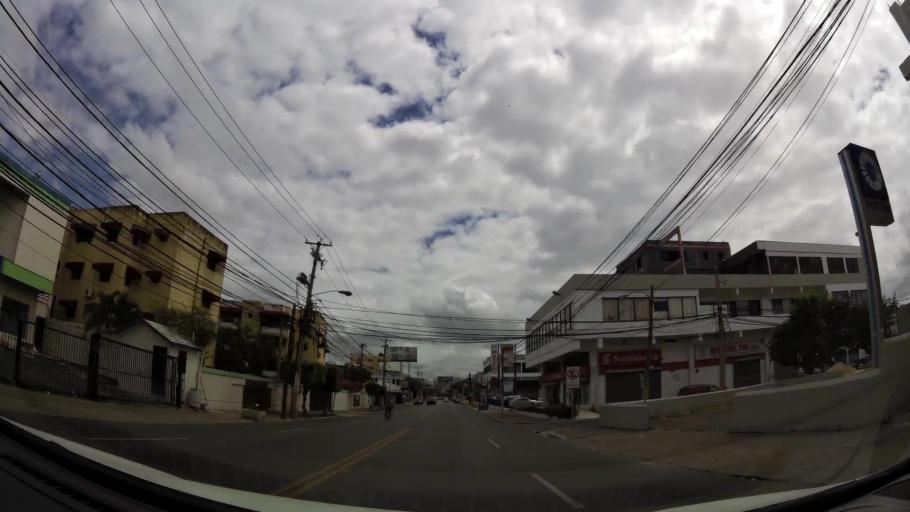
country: DO
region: Nacional
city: La Julia
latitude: 18.4768
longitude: -69.9518
